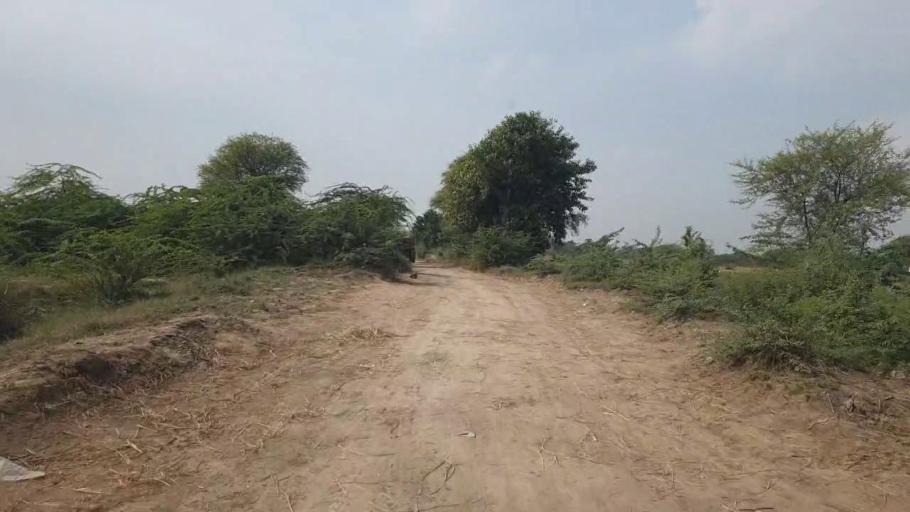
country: PK
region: Sindh
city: Talhar
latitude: 24.8851
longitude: 68.7998
